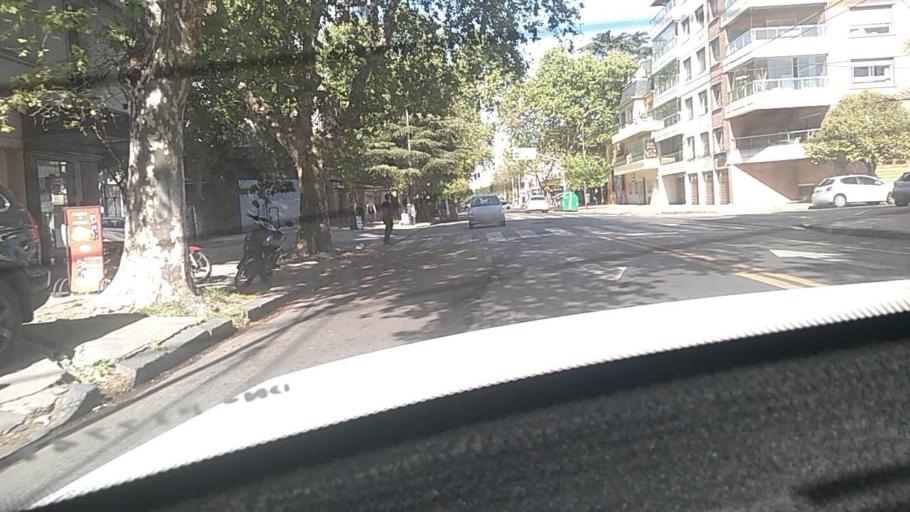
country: AR
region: Buenos Aires F.D.
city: Villa Santa Rita
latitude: -34.6029
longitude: -58.5072
